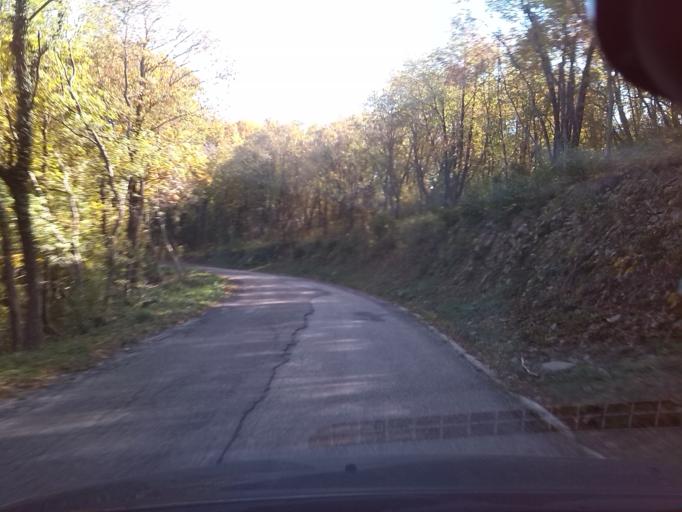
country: IT
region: Friuli Venezia Giulia
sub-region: Provincia di Udine
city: San Leonardo
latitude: 46.0994
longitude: 13.5435
